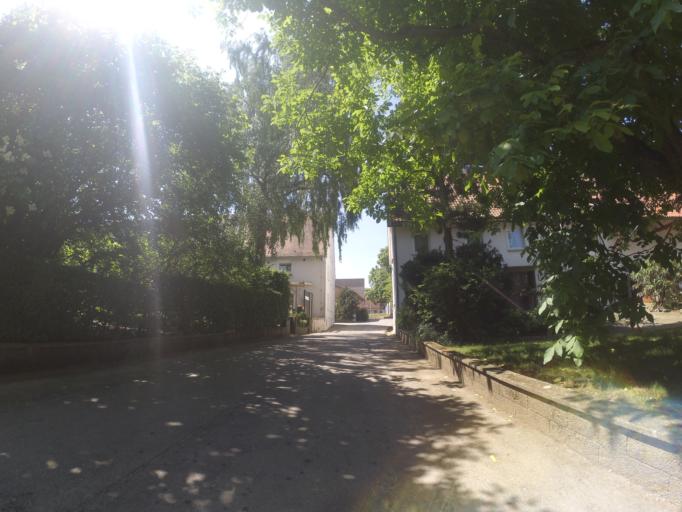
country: DE
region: Baden-Wuerttemberg
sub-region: Tuebingen Region
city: Bernstadt
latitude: 48.4742
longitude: 10.0186
